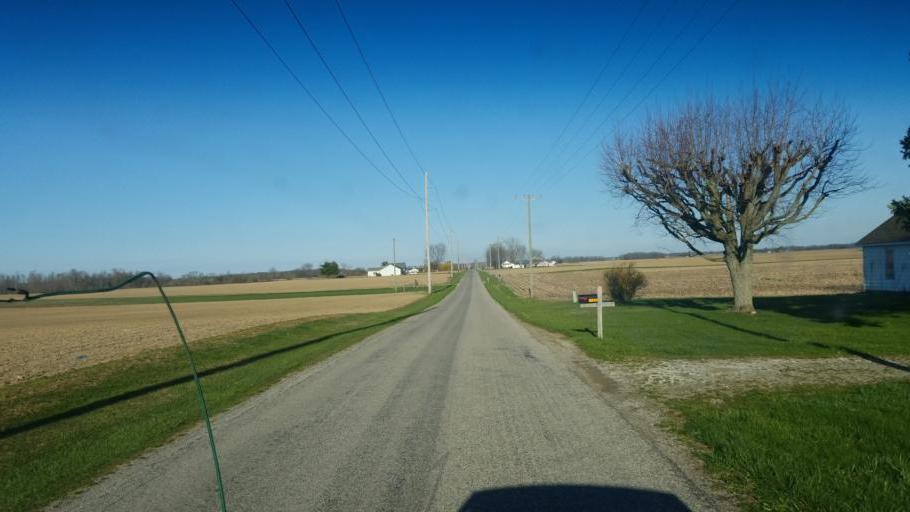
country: US
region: Ohio
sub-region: Union County
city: Richwood
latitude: 40.4483
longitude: -83.3979
